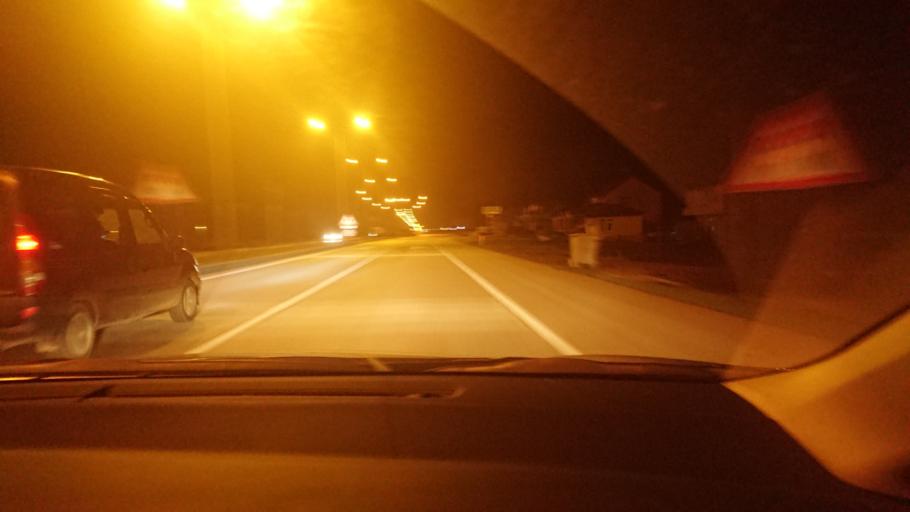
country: TR
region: Ordu
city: Ikizce
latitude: 41.1648
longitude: 37.0714
